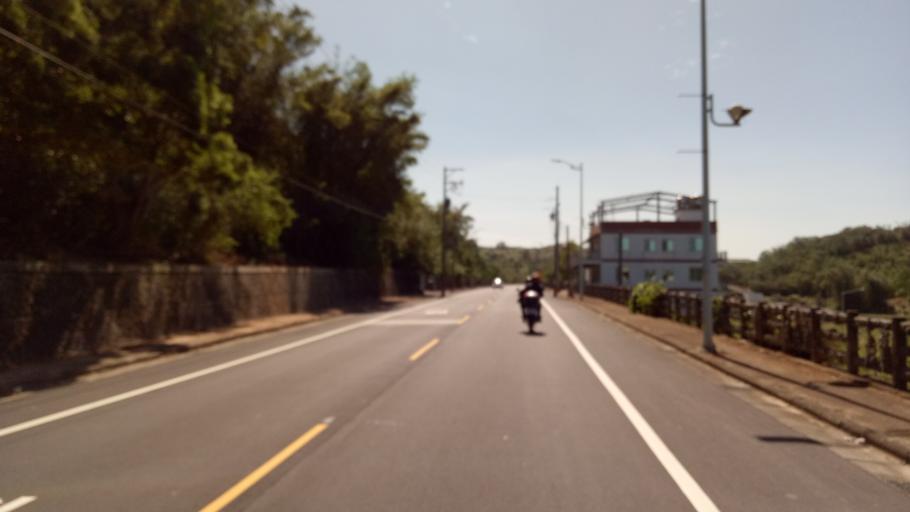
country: TW
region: Taiwan
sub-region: Hsinchu
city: Hsinchu
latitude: 24.7239
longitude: 120.9259
